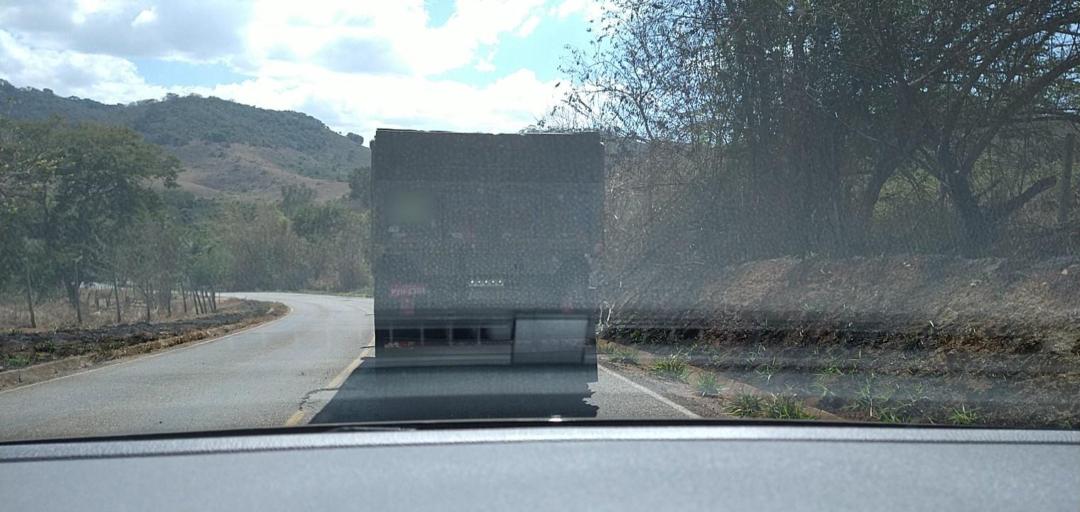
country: BR
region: Minas Gerais
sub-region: Ponte Nova
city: Ponte Nova
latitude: -20.2822
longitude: -42.9021
